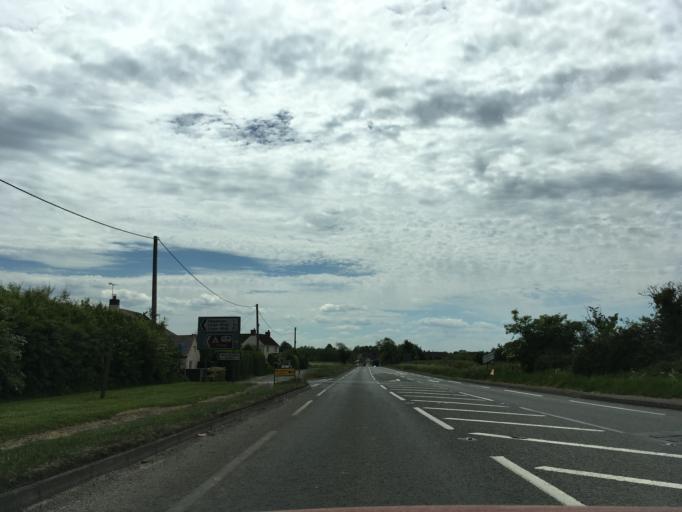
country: GB
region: England
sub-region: Gloucestershire
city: Berkeley
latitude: 51.6834
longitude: -2.4335
